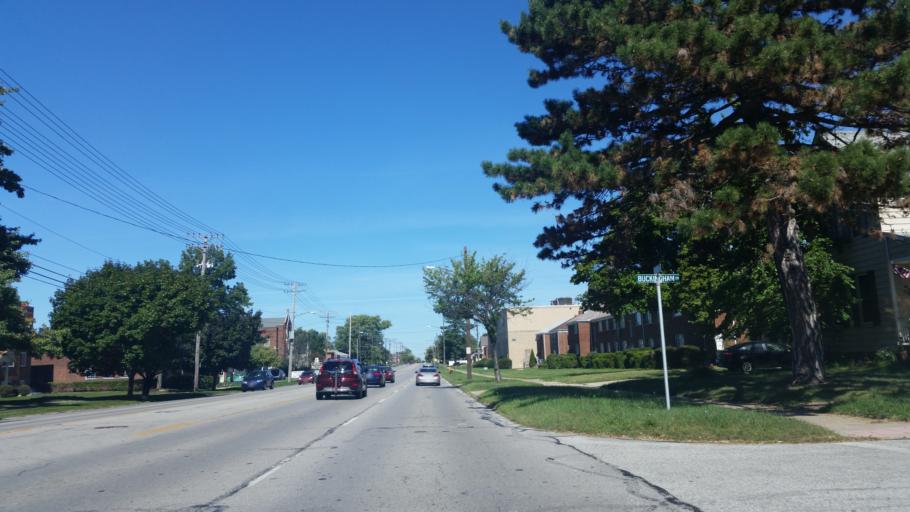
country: US
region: Ohio
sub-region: Cuyahoga County
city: Parma
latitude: 41.3894
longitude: -81.7345
